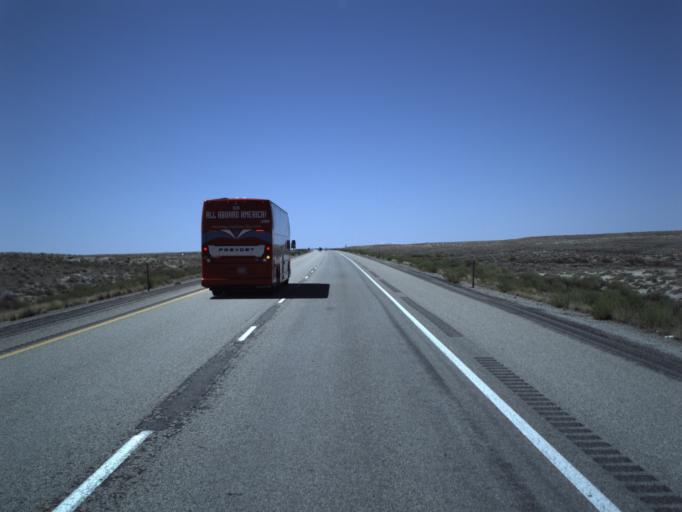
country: US
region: Utah
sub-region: Grand County
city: Moab
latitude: 38.9650
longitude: -109.3746
